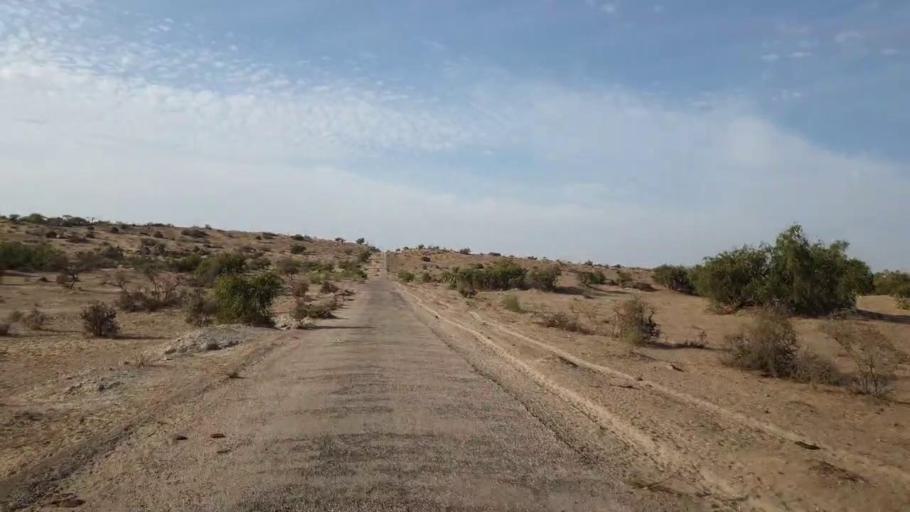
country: PK
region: Sindh
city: Nabisar
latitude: 25.0031
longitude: 69.9236
